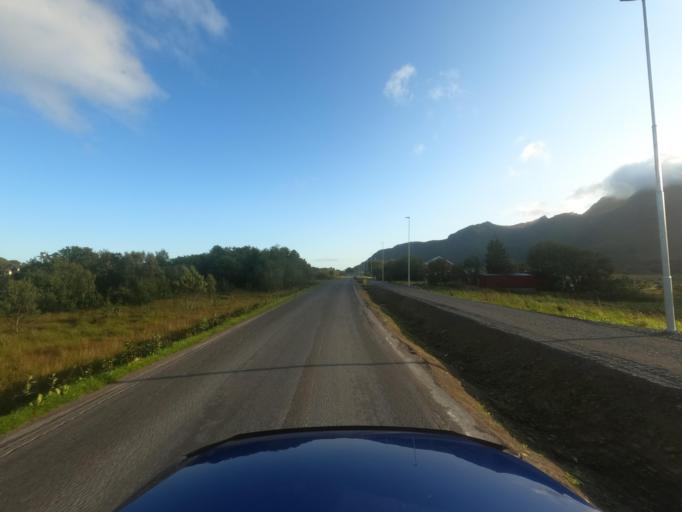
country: NO
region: Nordland
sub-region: Vestvagoy
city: Gravdal
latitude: 68.0949
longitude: 13.5452
